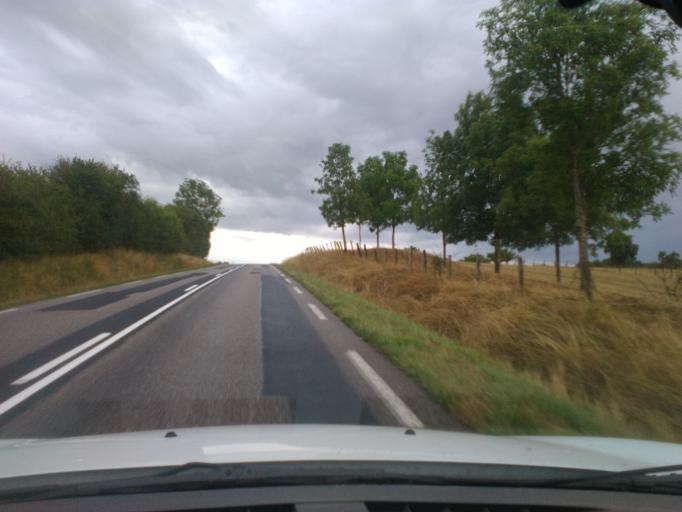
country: FR
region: Lorraine
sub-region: Departement de Meurthe-et-Moselle
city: Vezelise
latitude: 48.4269
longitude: 6.1259
